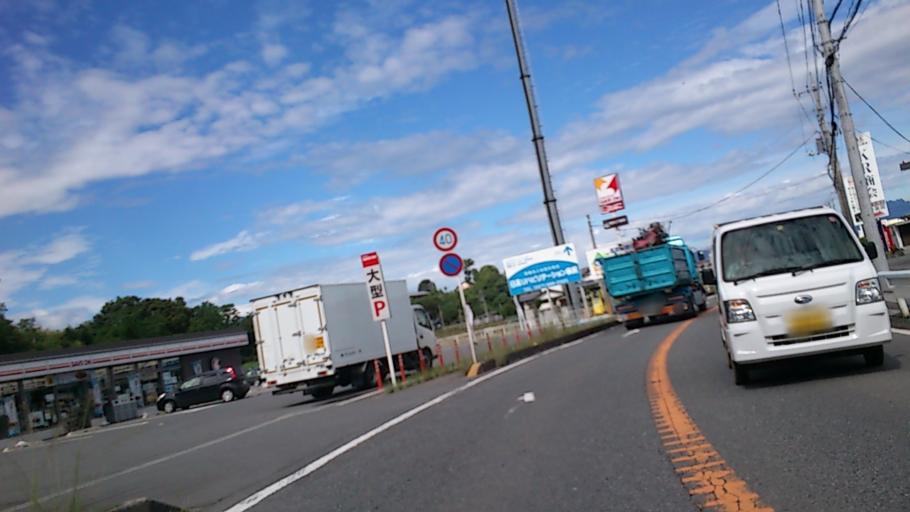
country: JP
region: Gunma
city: Yoshii
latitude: 36.2549
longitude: 139.0032
